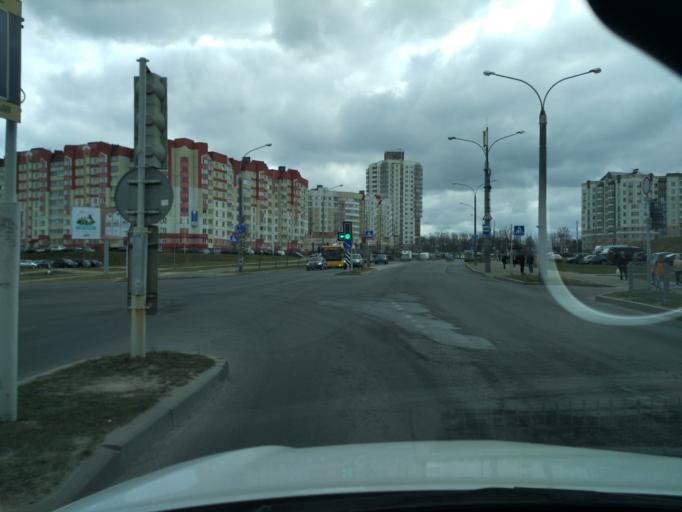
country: BY
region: Minsk
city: Shchomyslitsa
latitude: 53.8486
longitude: 27.4822
